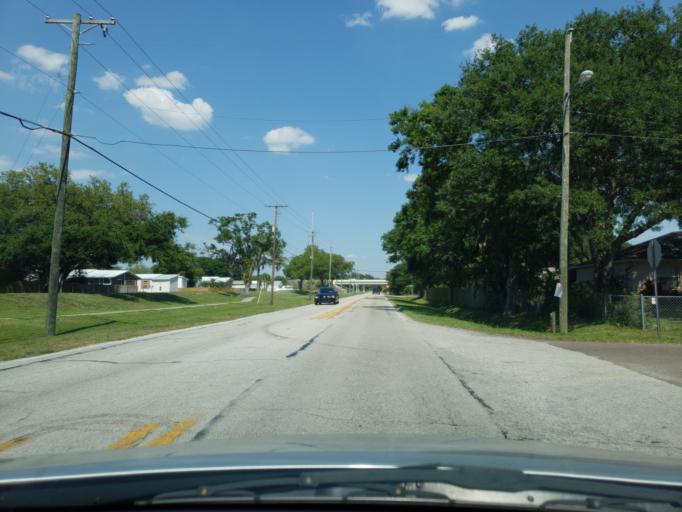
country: US
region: Florida
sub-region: Hillsborough County
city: Riverview
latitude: 27.8643
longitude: -82.3507
